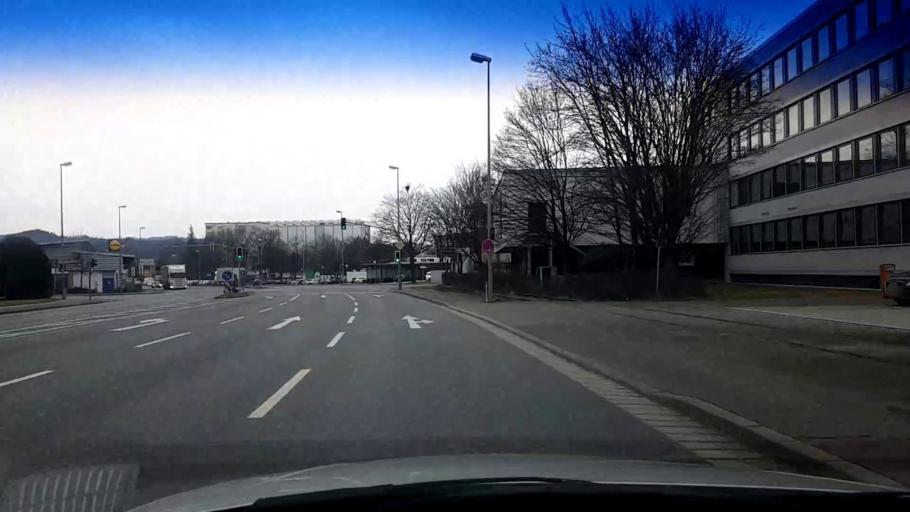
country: DE
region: Bavaria
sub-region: Upper Franconia
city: Kulmbach
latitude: 50.1021
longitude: 11.4416
